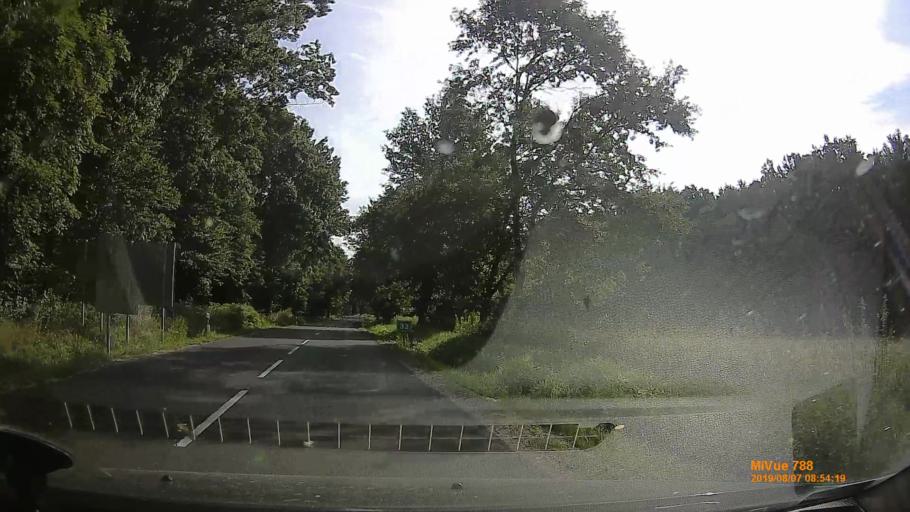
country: HU
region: Zala
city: Zalaegerszeg
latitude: 46.7304
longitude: 16.8624
